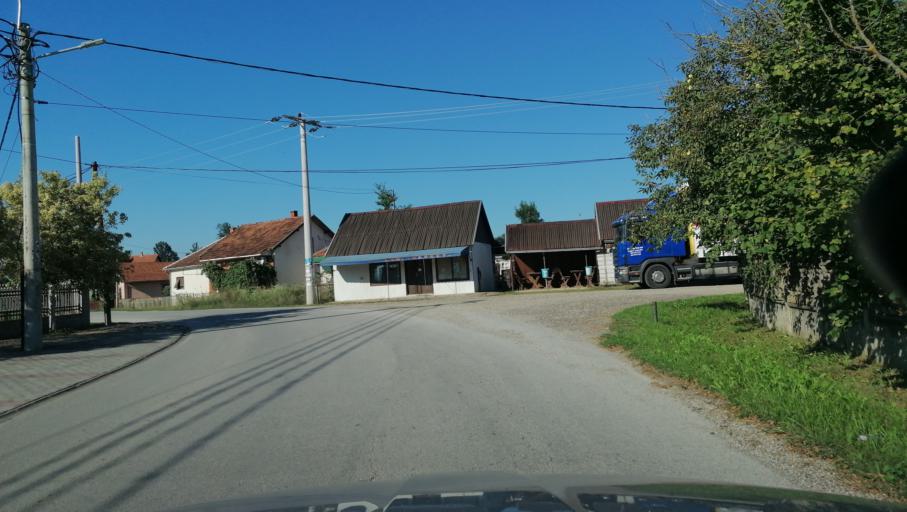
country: RS
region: Central Serbia
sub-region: Raski Okrug
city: Kraljevo
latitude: 43.8323
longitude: 20.5949
